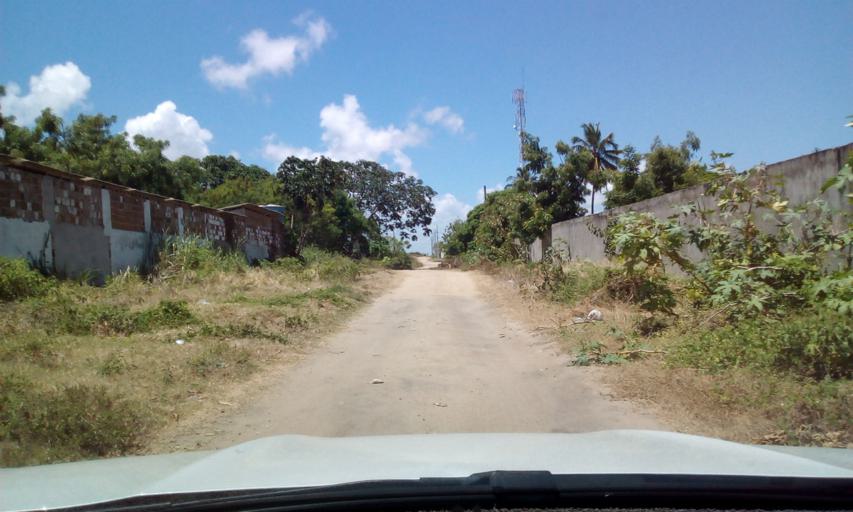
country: BR
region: Paraiba
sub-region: Joao Pessoa
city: Joao Pessoa
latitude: -7.1517
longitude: -34.8078
